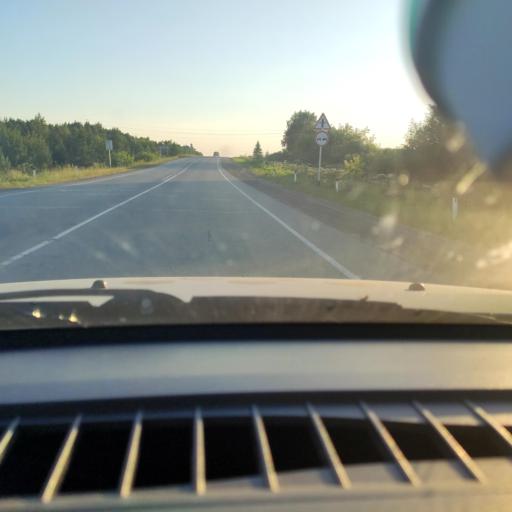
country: RU
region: Perm
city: Kungur
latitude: 57.4506
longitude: 57.0092
